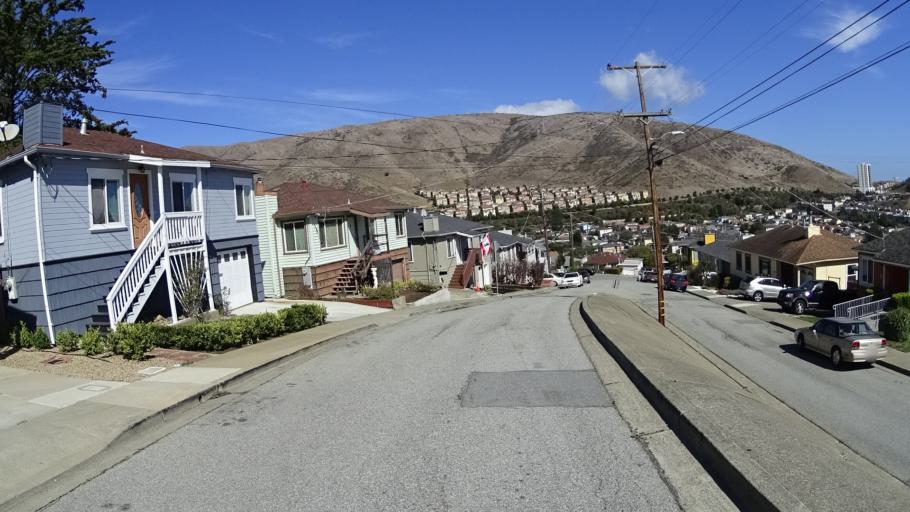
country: US
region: California
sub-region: San Mateo County
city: South San Francisco
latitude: 37.6636
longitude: -122.4137
